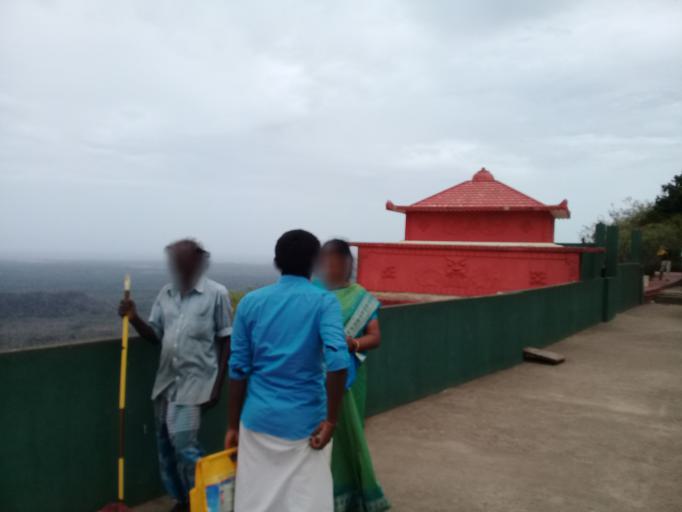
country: LK
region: Uva
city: Wattegama
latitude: 6.3874
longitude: 81.3363
